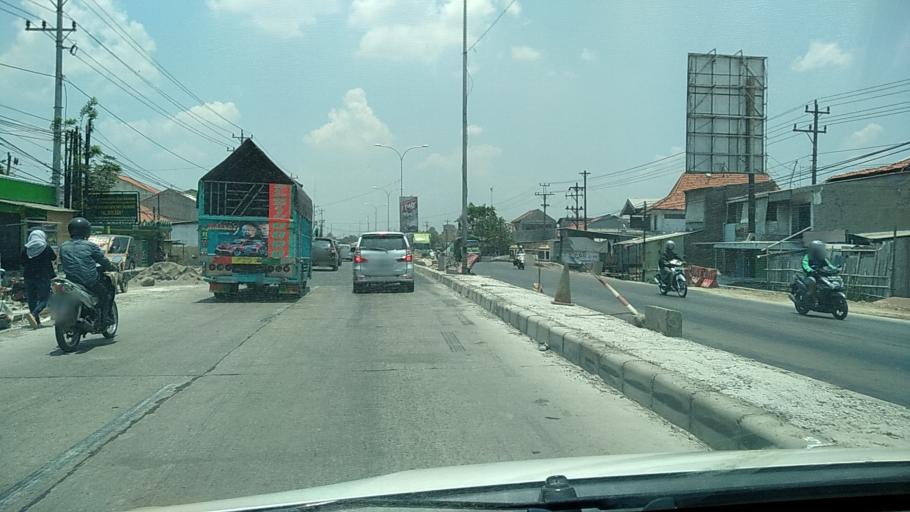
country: ID
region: Central Java
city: Semarang
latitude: -6.9552
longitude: 110.4701
